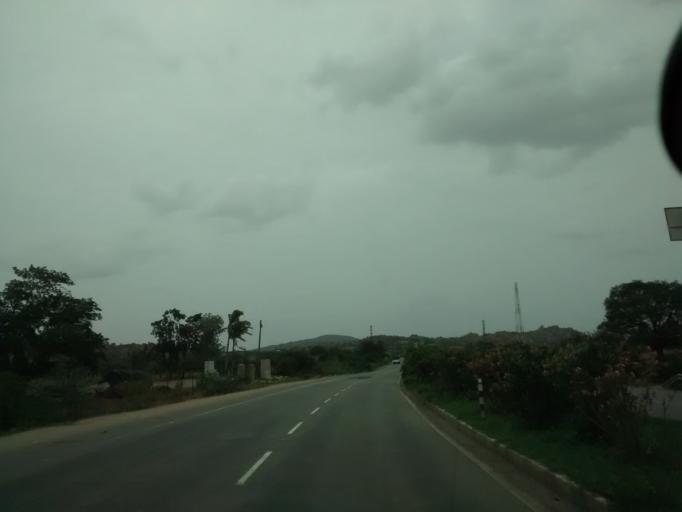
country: IN
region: Andhra Pradesh
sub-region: Kurnool
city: Ramapuram
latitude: 15.1971
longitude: 77.7042
